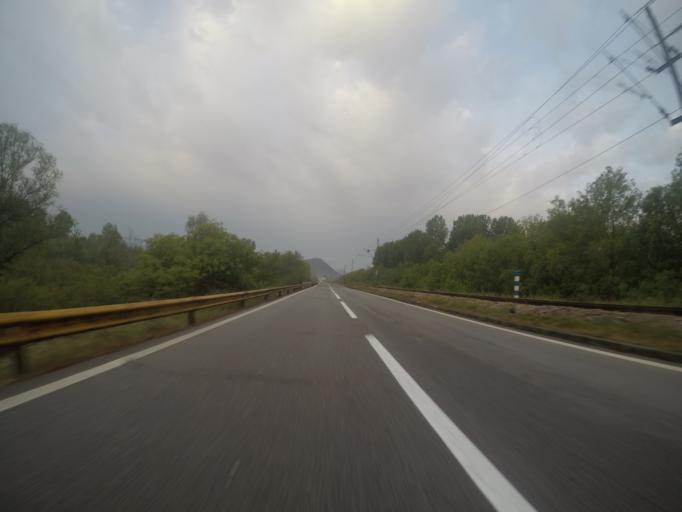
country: ME
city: Mojanovici
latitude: 42.2990
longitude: 19.1637
